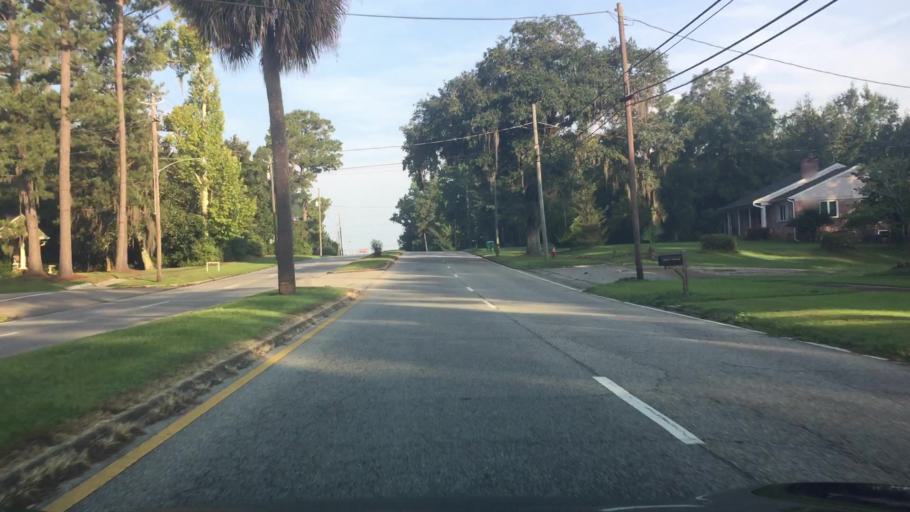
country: US
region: Alabama
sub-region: Covington County
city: Florala
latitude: 31.0013
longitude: -86.3192
